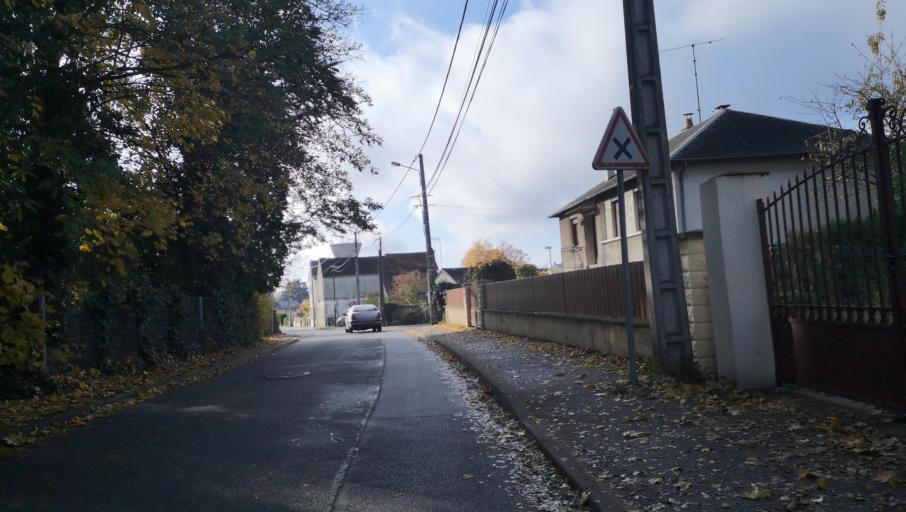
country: FR
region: Centre
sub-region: Departement du Loiret
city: Semoy
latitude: 47.9125
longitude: 1.9385
